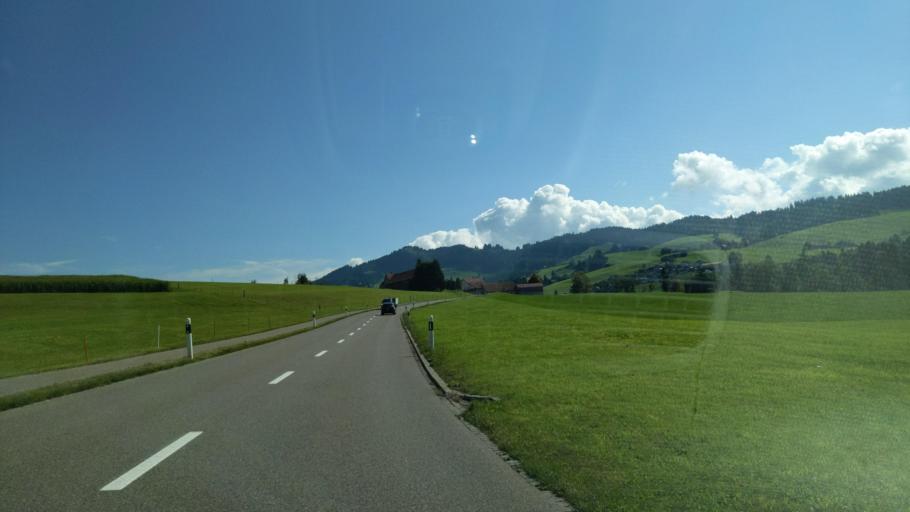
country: CH
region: Saint Gallen
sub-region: Wahlkreis Toggenburg
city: Sankt Peterzell
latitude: 47.3205
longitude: 9.1962
